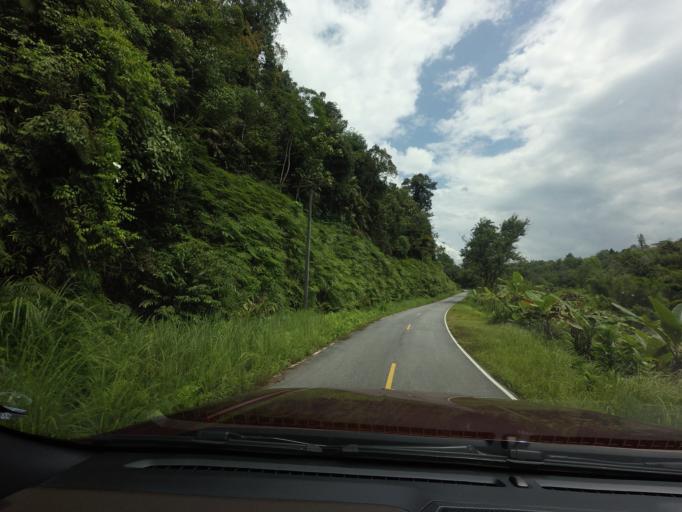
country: TH
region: Narathiwat
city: Sukhirin
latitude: 5.9389
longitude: 101.6516
